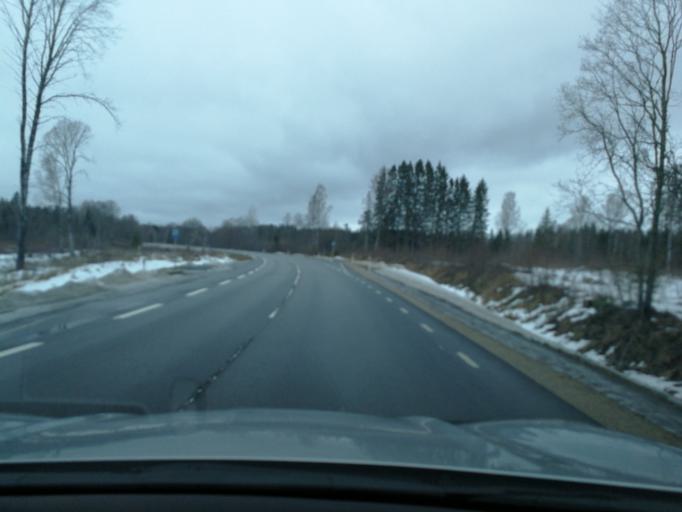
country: EE
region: Harju
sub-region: Anija vald
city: Kehra
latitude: 59.2920
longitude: 25.3757
